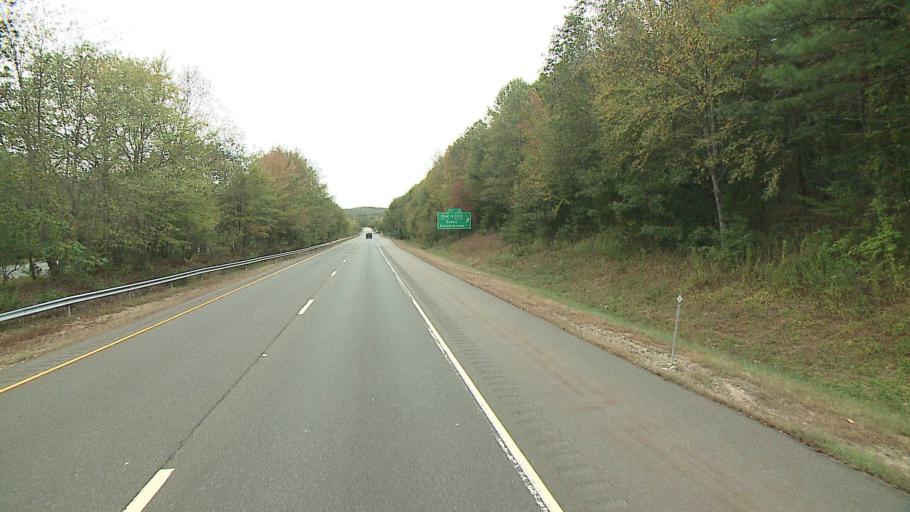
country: US
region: Connecticut
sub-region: Middlesex County
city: Essex Village
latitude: 41.3449
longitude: -72.3995
